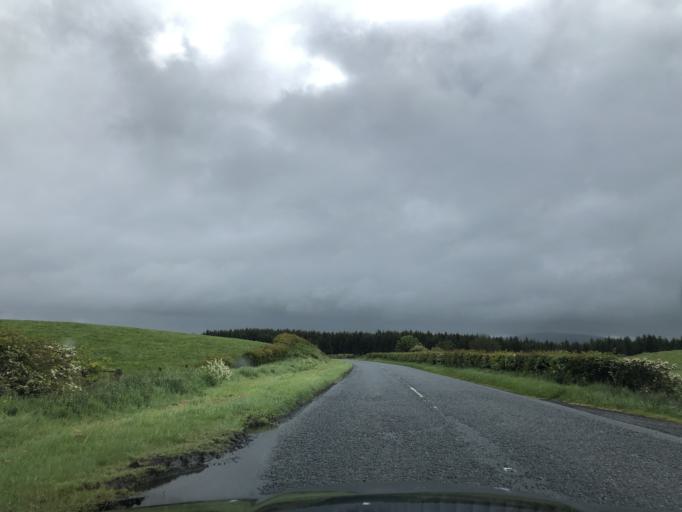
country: GB
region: Northern Ireland
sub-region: Moyle District
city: Ballycastle
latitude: 55.1623
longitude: -6.3697
